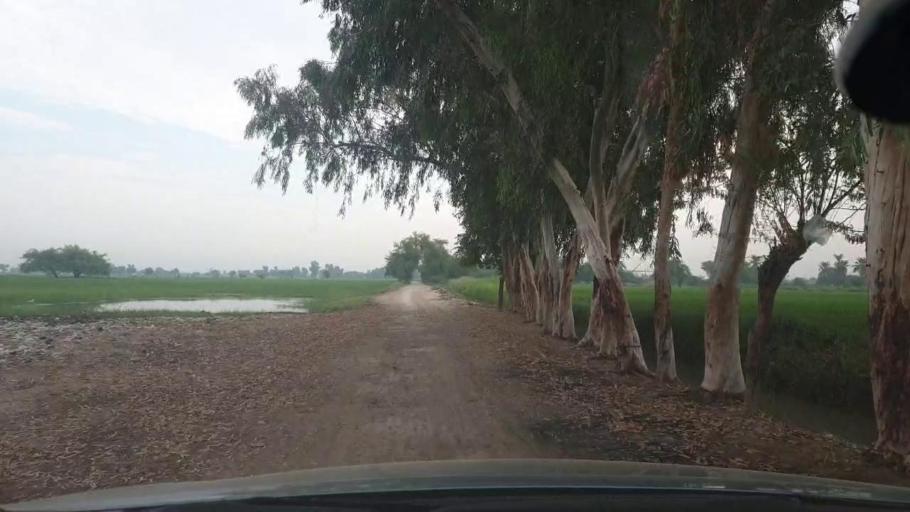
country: PK
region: Sindh
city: Jacobabad
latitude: 28.2950
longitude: 68.4217
